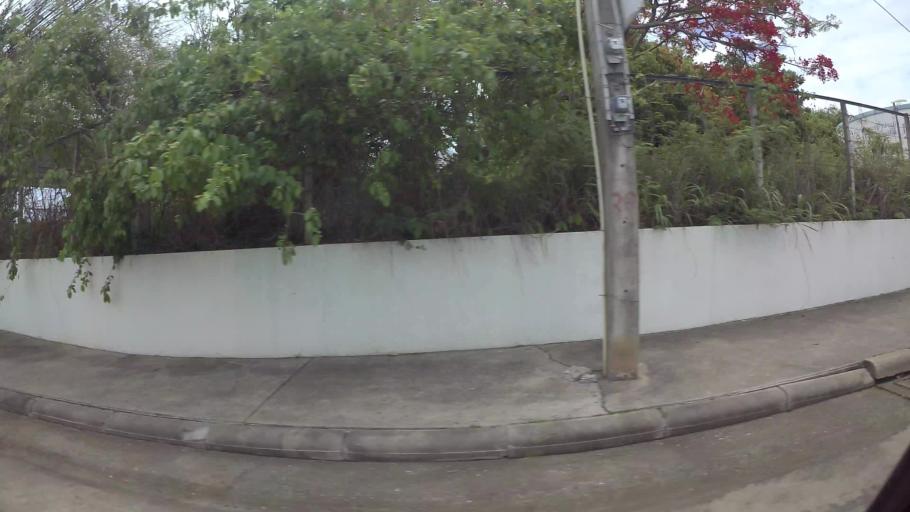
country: TH
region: Chon Buri
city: Sattahip
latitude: 12.7610
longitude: 100.9005
